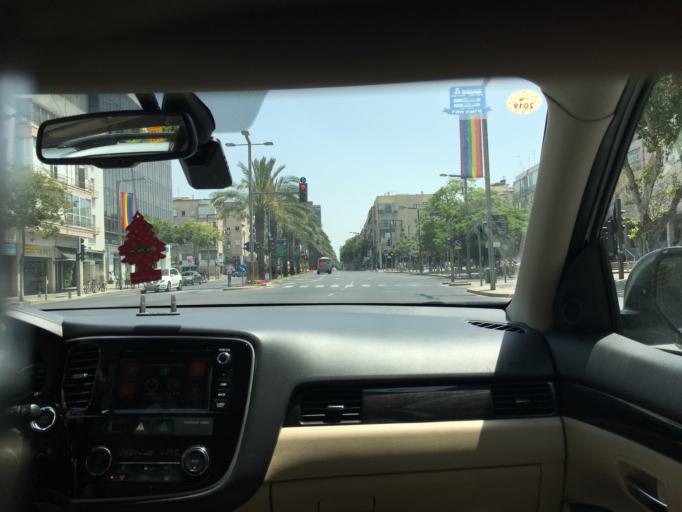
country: IL
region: Tel Aviv
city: Tel Aviv
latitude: 32.0919
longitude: 34.7829
